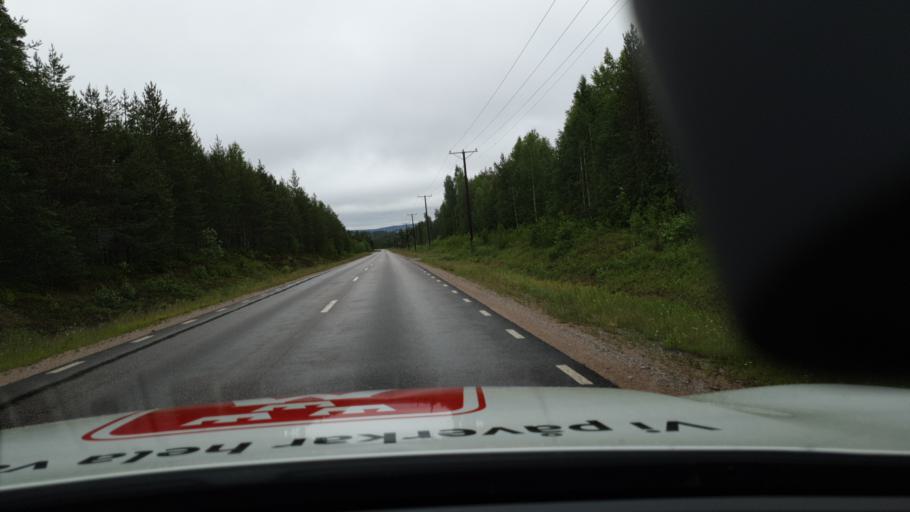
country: SE
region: Norrbotten
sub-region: Overtornea Kommun
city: OEvertornea
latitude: 66.3972
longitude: 23.5831
